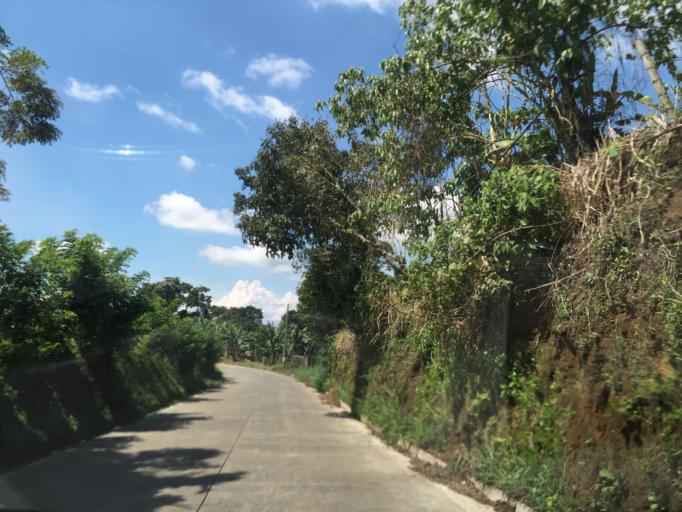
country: CO
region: Valle del Cauca
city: Ulloa
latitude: 4.6998
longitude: -75.7513
